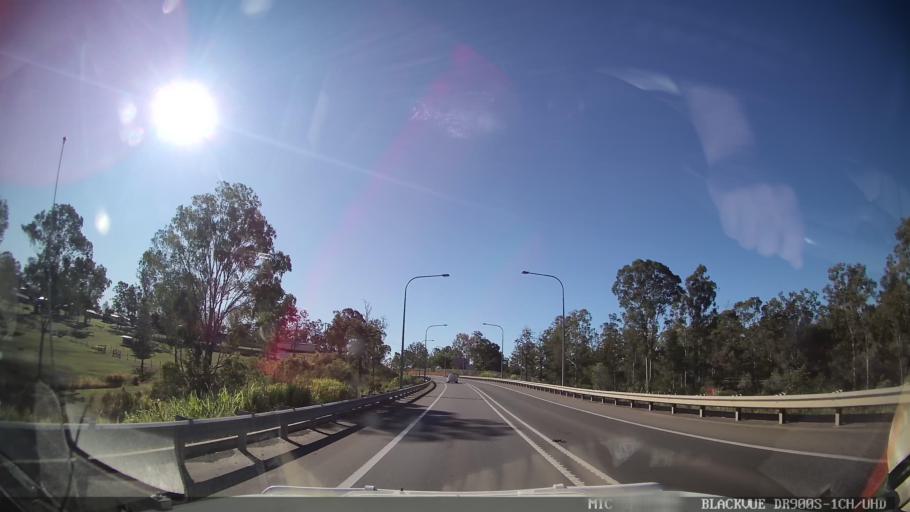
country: AU
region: Queensland
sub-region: Bundaberg
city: Sharon
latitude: -24.9979
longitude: 151.9608
